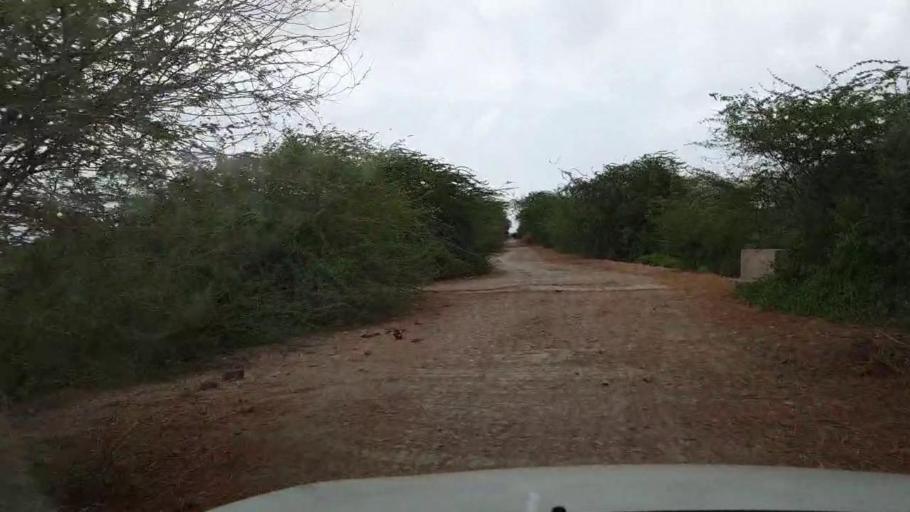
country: PK
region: Sindh
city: Kario
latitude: 24.6880
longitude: 68.6666
